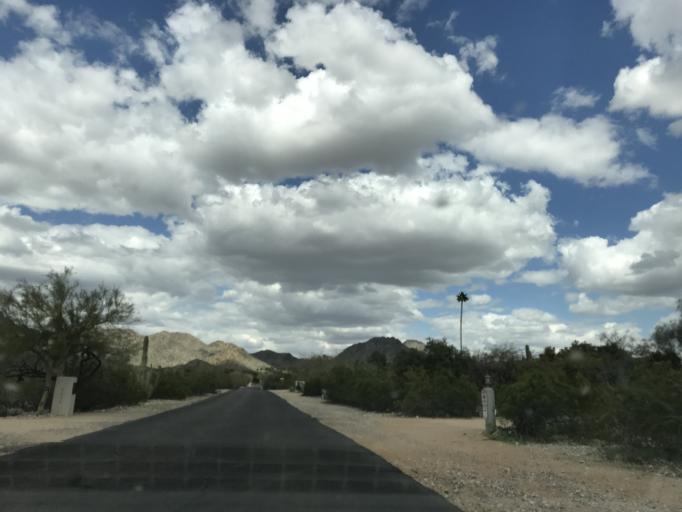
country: US
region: Arizona
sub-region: Maricopa County
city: Paradise Valley
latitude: 33.5183
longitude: -112.0067
